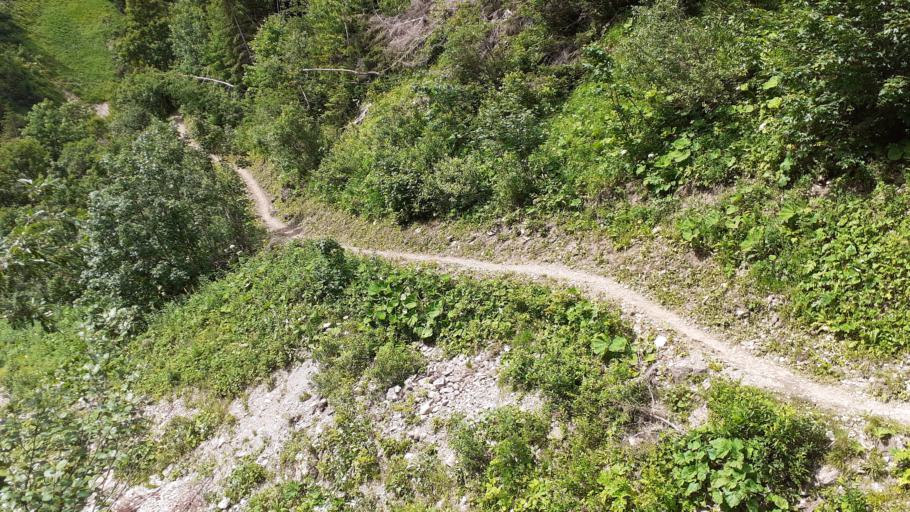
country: AT
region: Vorarlberg
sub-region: Politischer Bezirk Bregenz
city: Warth
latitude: 47.2451
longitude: 10.1786
